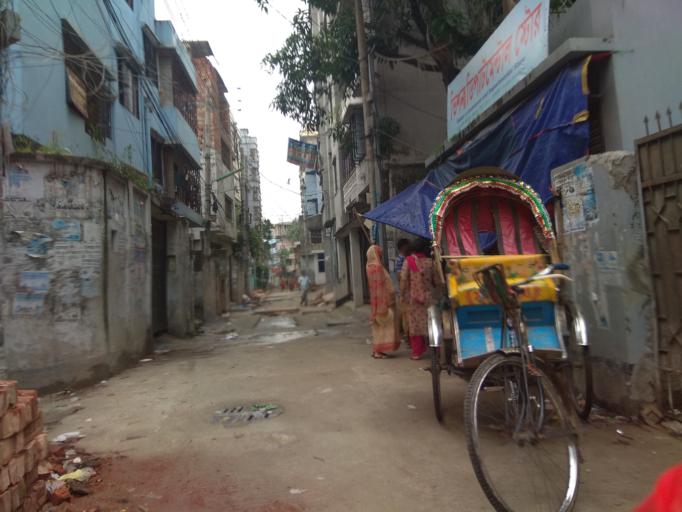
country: BD
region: Dhaka
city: Azimpur
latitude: 23.7958
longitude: 90.3674
